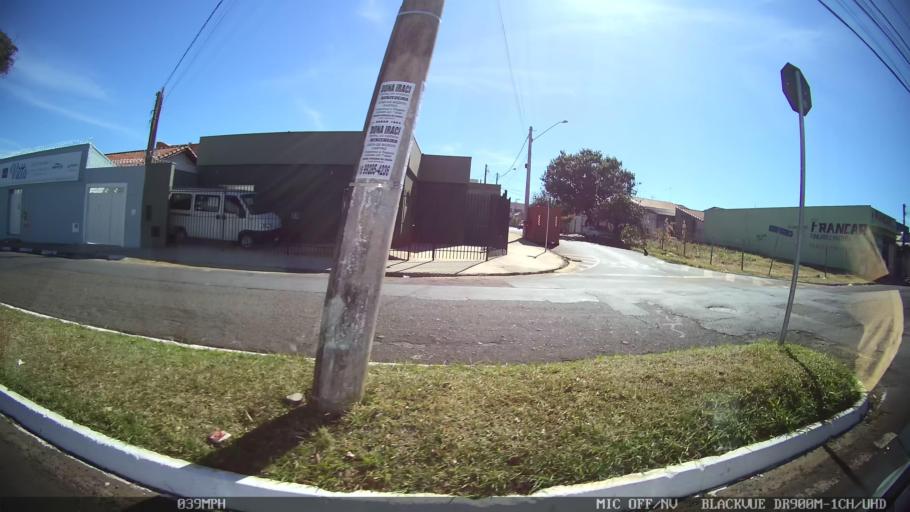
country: BR
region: Sao Paulo
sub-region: Franca
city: Franca
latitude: -20.5403
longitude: -47.3647
